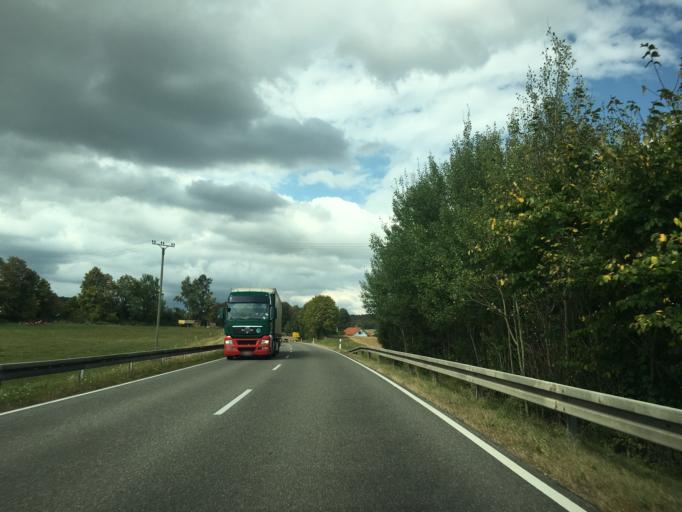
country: DE
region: Baden-Wuerttemberg
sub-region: Tuebingen Region
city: Gomadingen
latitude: 48.3532
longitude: 9.3319
